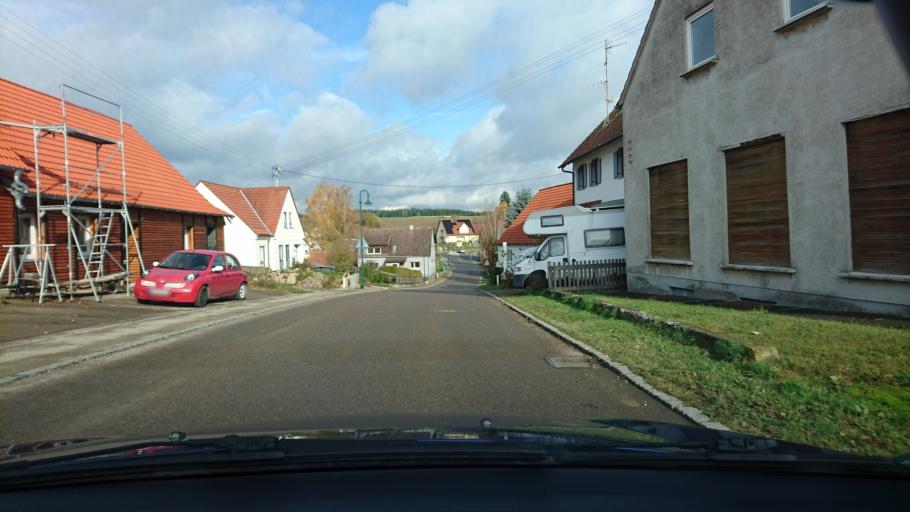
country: DE
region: Bavaria
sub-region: Swabia
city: Amerdingen
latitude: 48.7262
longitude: 10.4850
